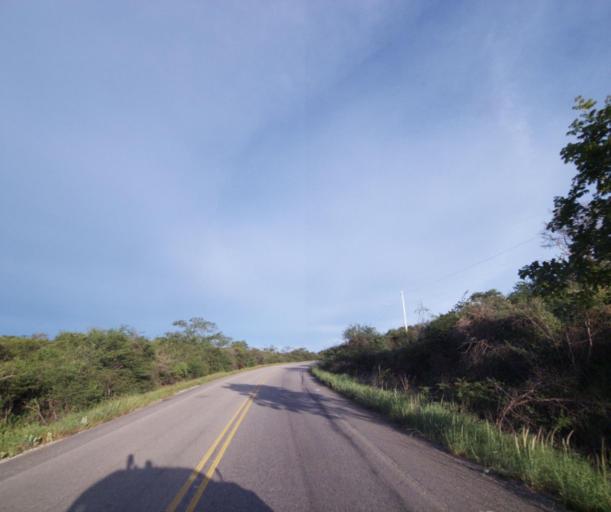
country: BR
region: Bahia
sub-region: Cacule
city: Cacule
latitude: -14.2071
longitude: -42.0704
